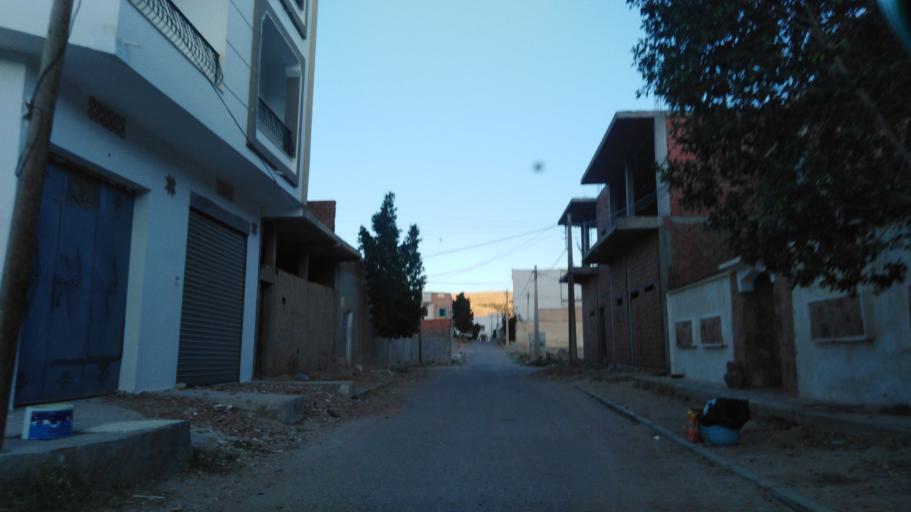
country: TN
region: Tataouine
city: Tataouine
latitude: 32.9418
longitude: 10.4544
